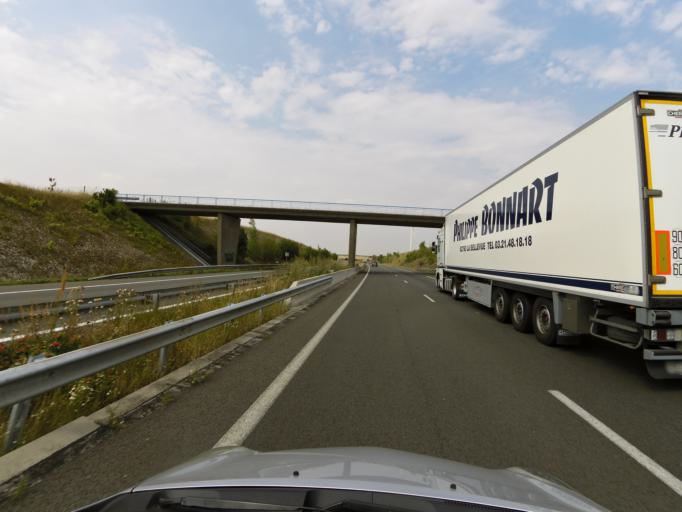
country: FR
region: Picardie
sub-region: Departement de l'Aisne
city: Holnon
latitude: 49.8891
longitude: 3.2551
